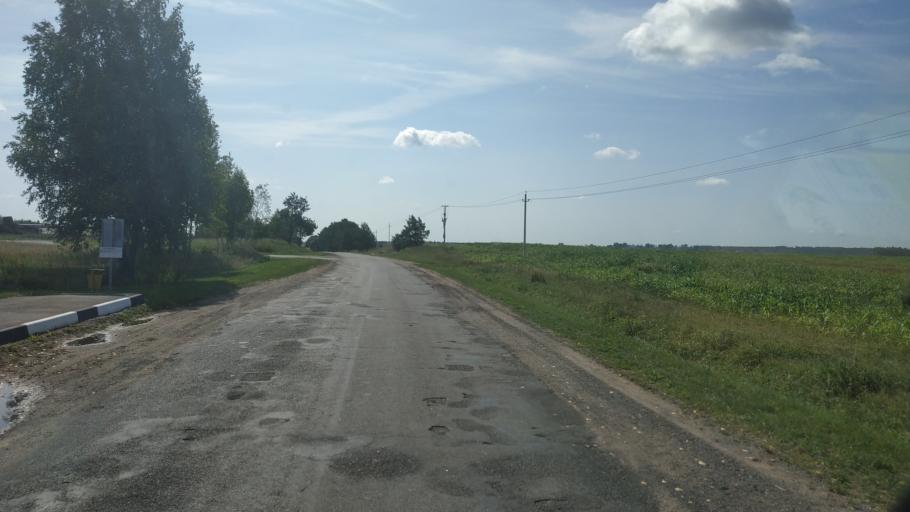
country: BY
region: Mogilev
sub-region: Mahilyowski Rayon
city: Veyno
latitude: 53.7848
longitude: 30.4352
